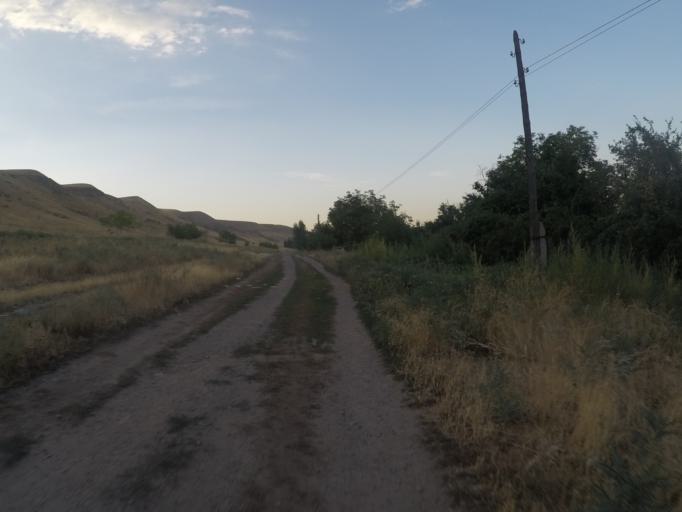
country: KG
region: Chuy
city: Bishkek
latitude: 42.7680
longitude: 74.6387
